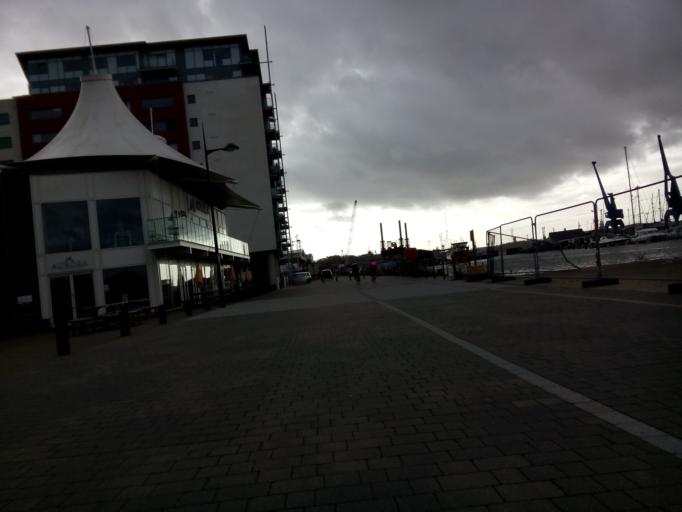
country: GB
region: England
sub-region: Suffolk
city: Ipswich
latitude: 52.0491
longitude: 1.1635
